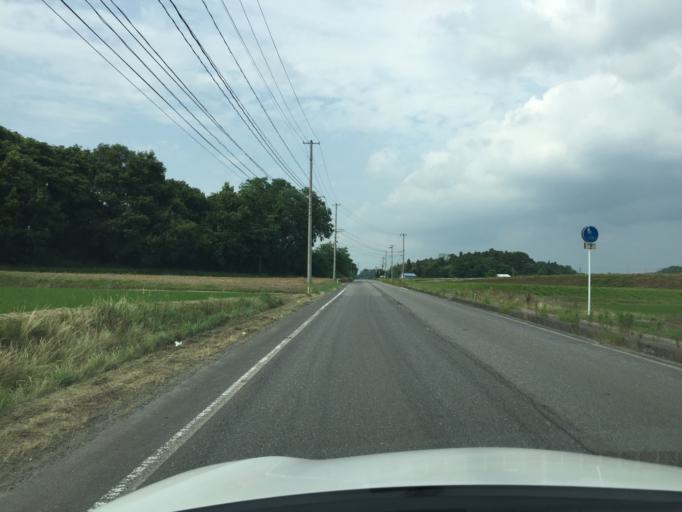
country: JP
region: Fukushima
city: Sukagawa
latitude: 37.2789
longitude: 140.4229
